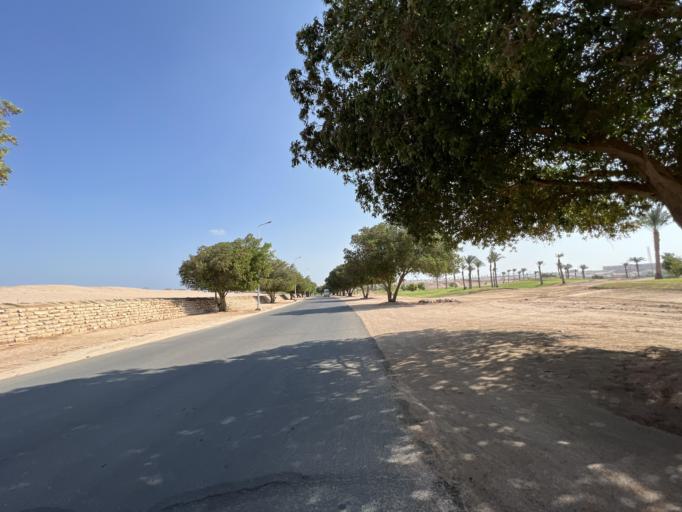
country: EG
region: Red Sea
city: Makadi Bay
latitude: 26.9855
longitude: 33.8888
